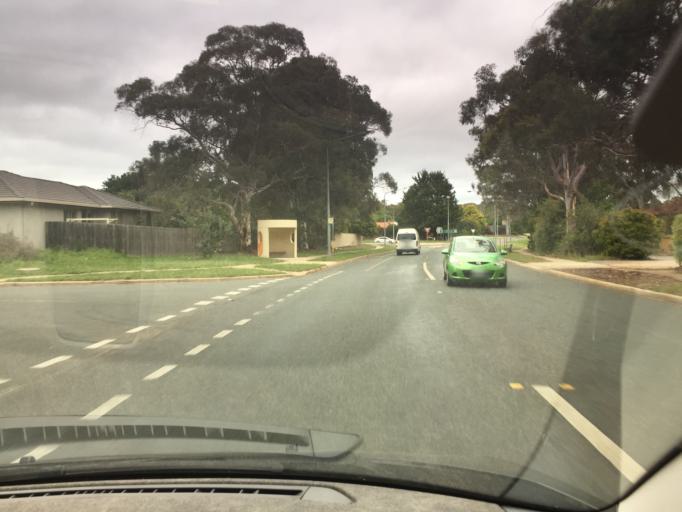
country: AU
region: Australian Capital Territory
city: Kaleen
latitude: -35.2289
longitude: 149.1113
